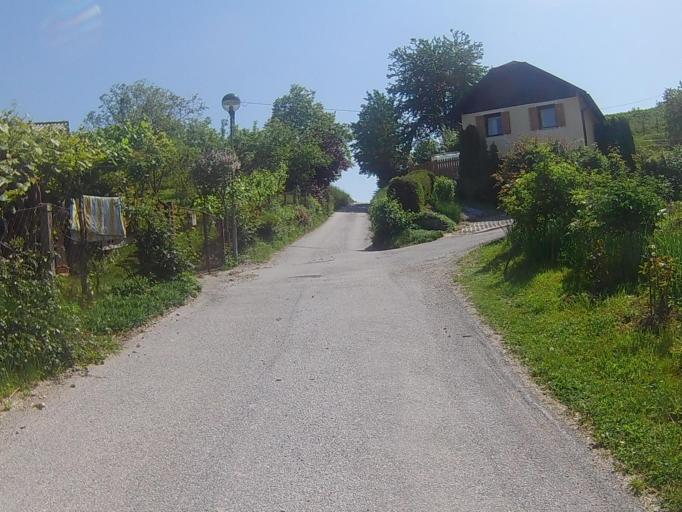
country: SI
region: Pesnica
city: Pesnica pri Mariboru
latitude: 46.5771
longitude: 15.7190
